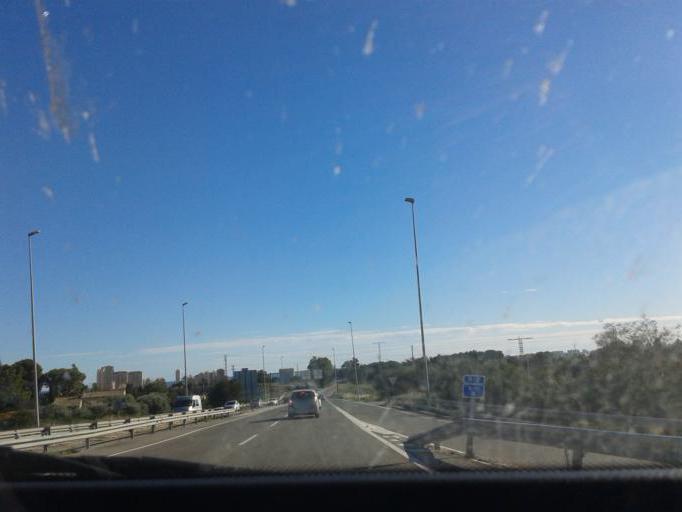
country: ES
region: Valencia
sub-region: Provincia de Alicante
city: San Juan de Alicante
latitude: 38.4182
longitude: -0.4248
